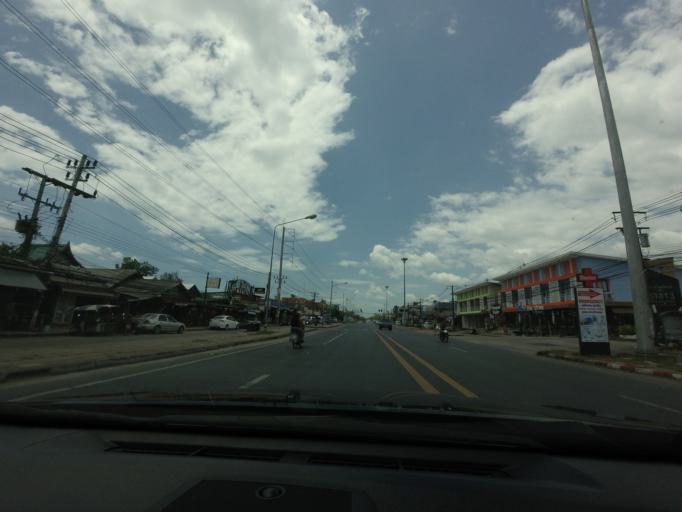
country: TH
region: Phangnga
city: Ban Khao Lak
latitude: 8.6662
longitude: 98.2531
